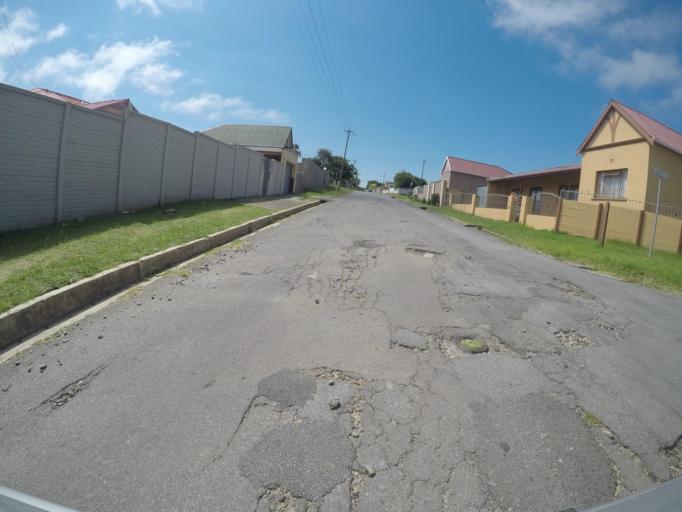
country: ZA
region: Eastern Cape
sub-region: Buffalo City Metropolitan Municipality
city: East London
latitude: -32.9790
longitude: 27.8930
